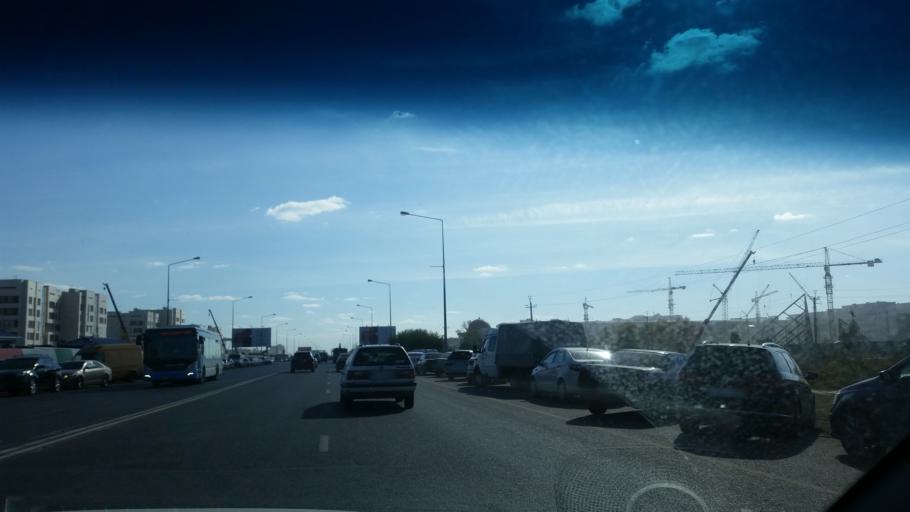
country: KZ
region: Astana Qalasy
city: Astana
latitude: 51.0961
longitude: 71.4051
